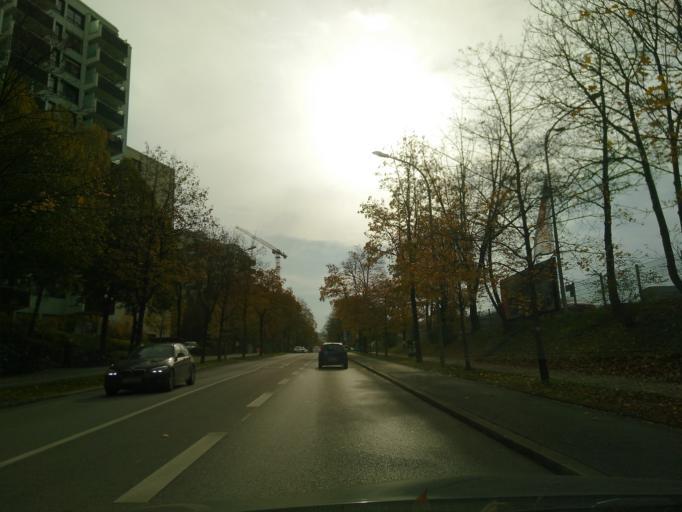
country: DE
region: Bavaria
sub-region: Upper Bavaria
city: Munich
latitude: 48.1223
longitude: 11.5984
